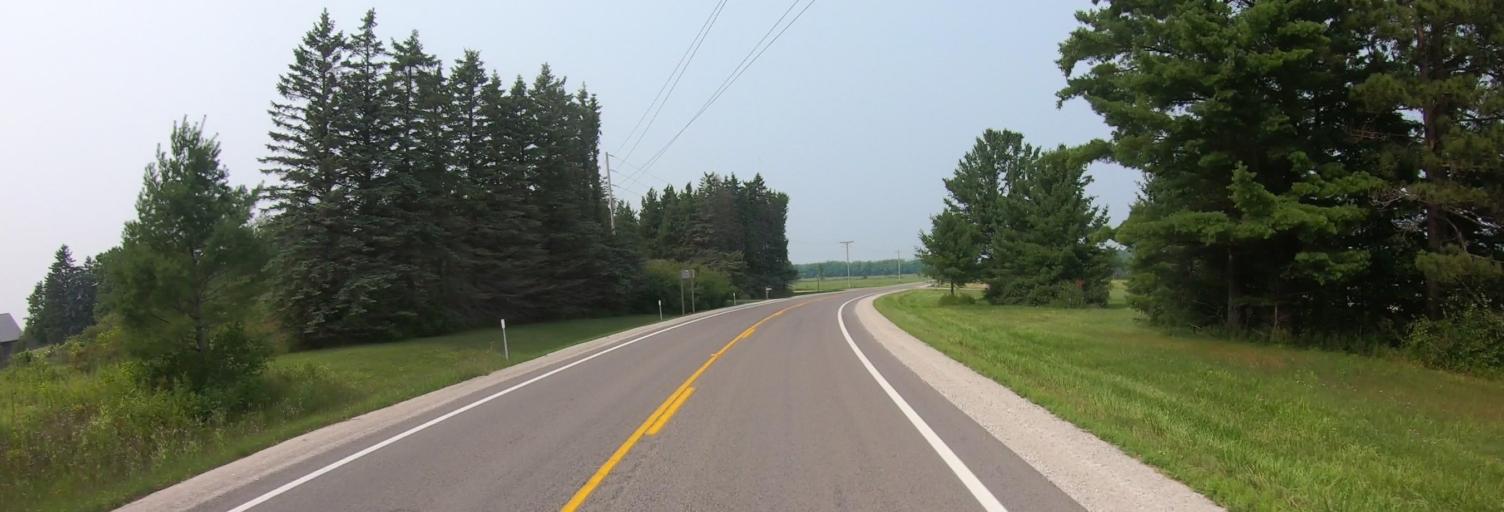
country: US
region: Michigan
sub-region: Chippewa County
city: Sault Ste. Marie
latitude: 46.0423
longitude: -84.0923
